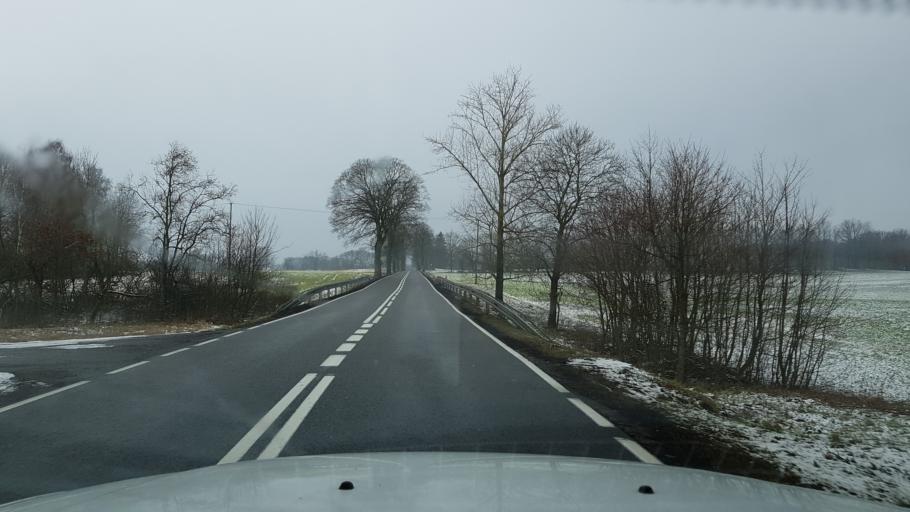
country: PL
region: West Pomeranian Voivodeship
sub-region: Powiat drawski
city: Czaplinek
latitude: 53.5599
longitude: 16.1807
